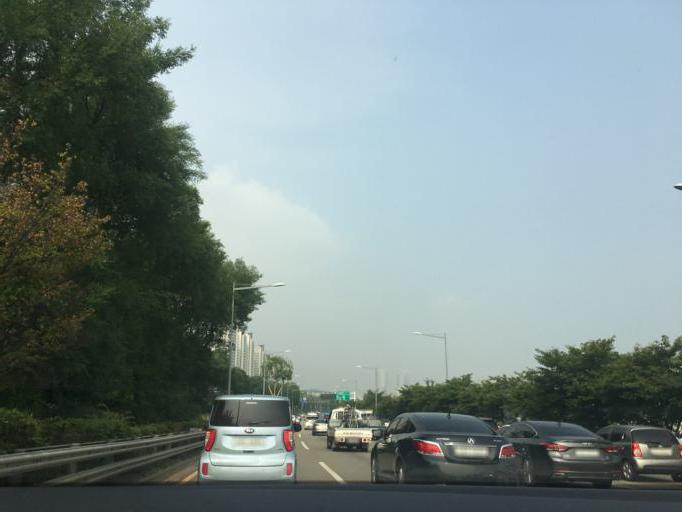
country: KR
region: Gyeonggi-do
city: Seongnam-si
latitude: 37.5173
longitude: 127.0881
